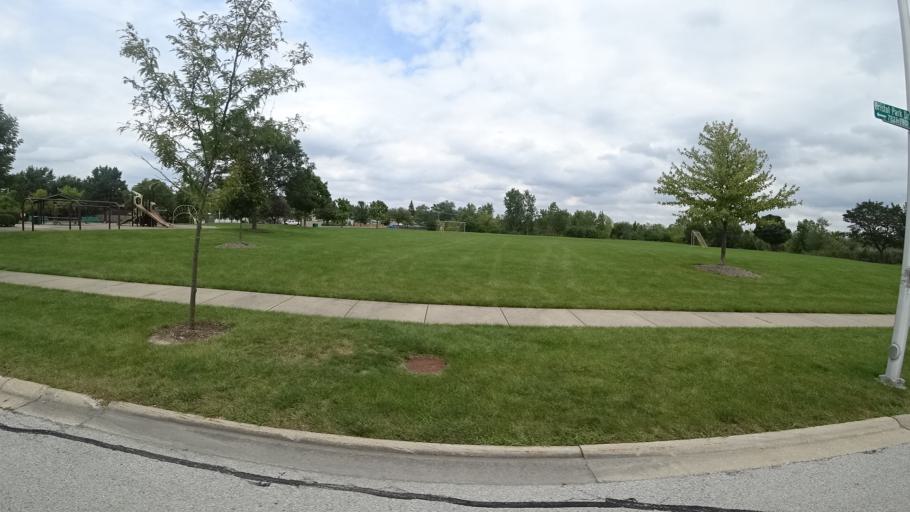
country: US
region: Illinois
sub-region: Cook County
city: Tinley Park
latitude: 41.5720
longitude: -87.8051
